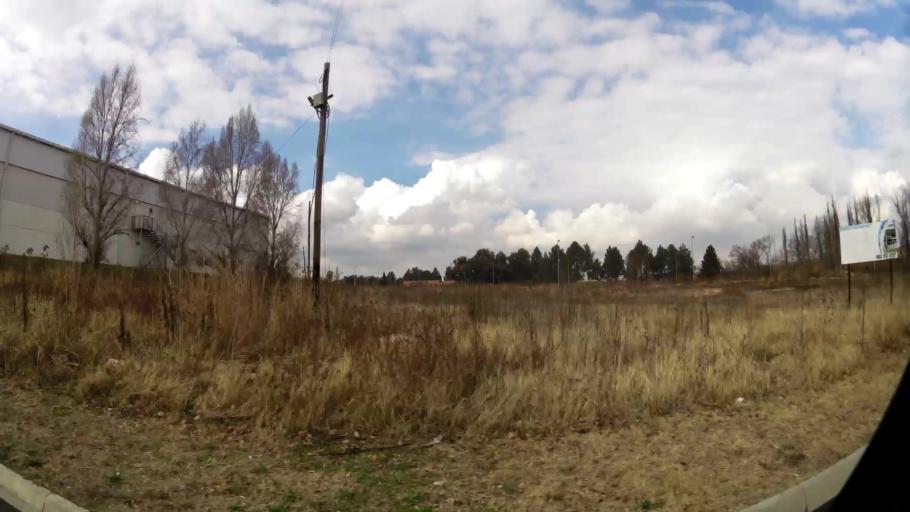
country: ZA
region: Gauteng
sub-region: Sedibeng District Municipality
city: Vanderbijlpark
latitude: -26.7416
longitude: 27.8430
